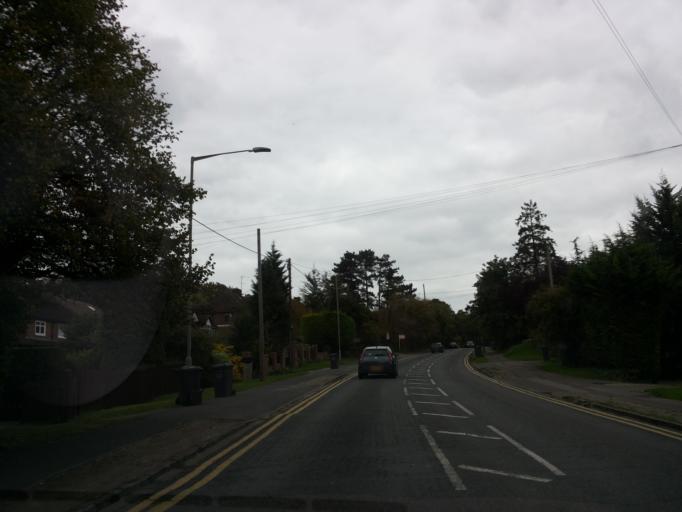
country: GB
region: England
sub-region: Buckinghamshire
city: Amersham on the Hill
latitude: 51.6644
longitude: -0.6001
